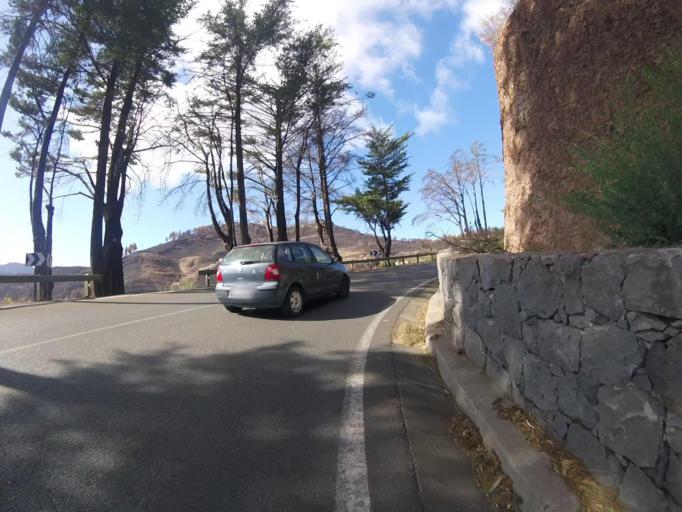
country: ES
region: Canary Islands
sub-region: Provincia de Las Palmas
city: Tejeda
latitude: 28.0080
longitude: -15.5921
